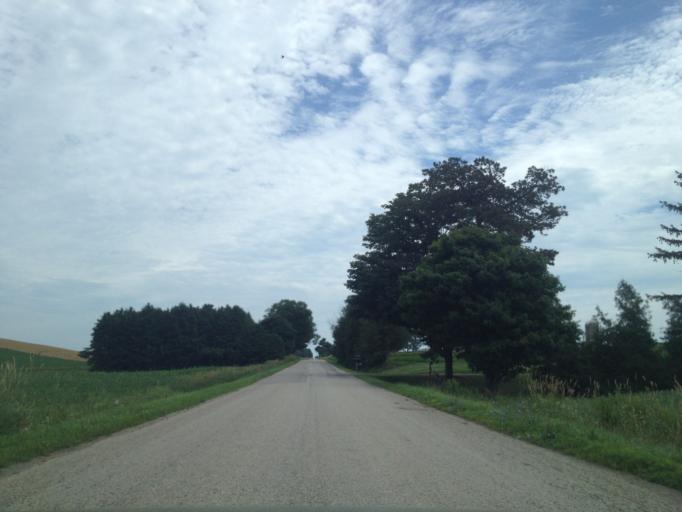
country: CA
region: Ontario
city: Ingersoll
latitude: 42.9768
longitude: -80.7690
